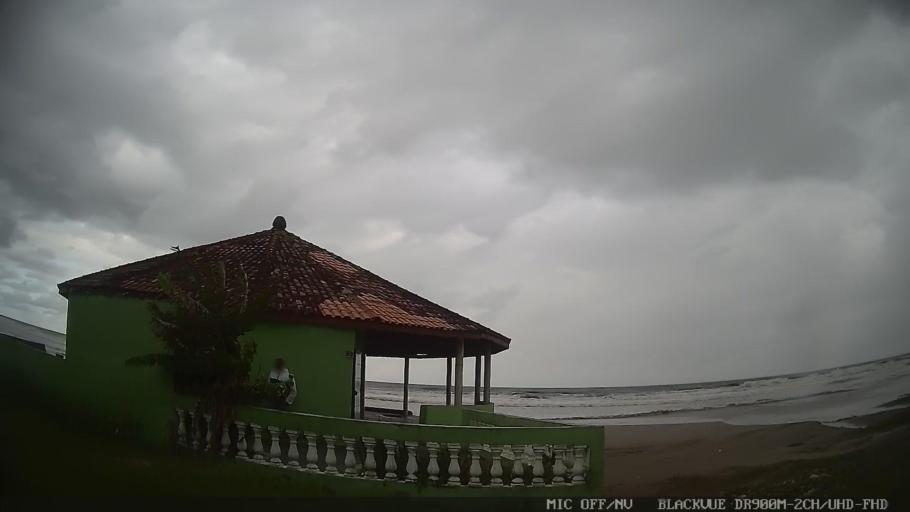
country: BR
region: Sao Paulo
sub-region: Itanhaem
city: Itanhaem
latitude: -24.1441
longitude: -46.7119
